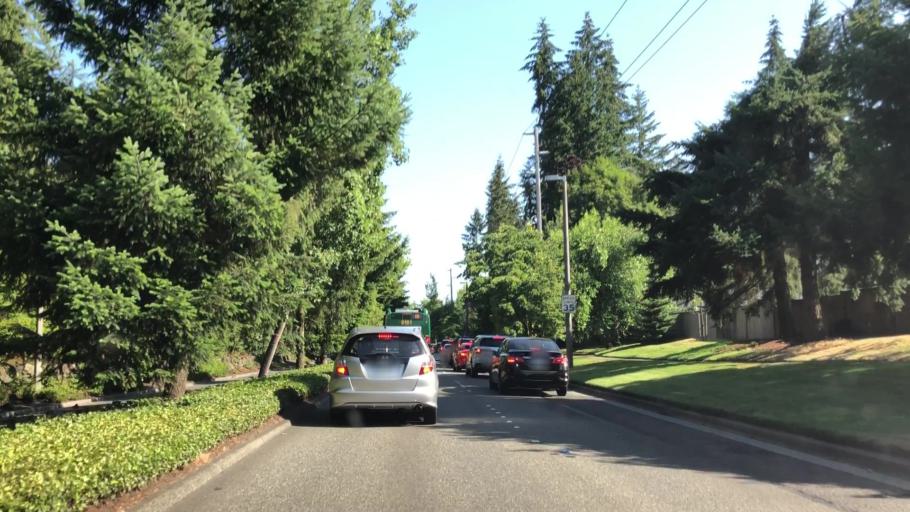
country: US
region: Washington
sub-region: King County
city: Eastgate
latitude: 47.5929
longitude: -122.1426
